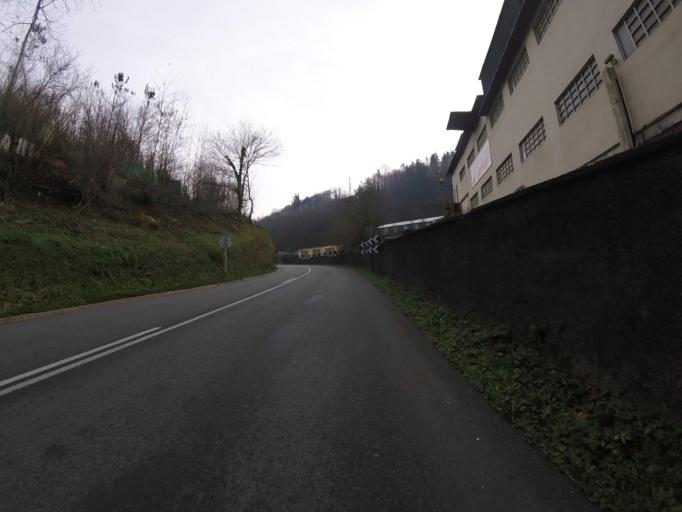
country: ES
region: Basque Country
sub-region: Provincia de Guipuzcoa
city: Berrobi
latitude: 43.1418
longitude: -2.0380
